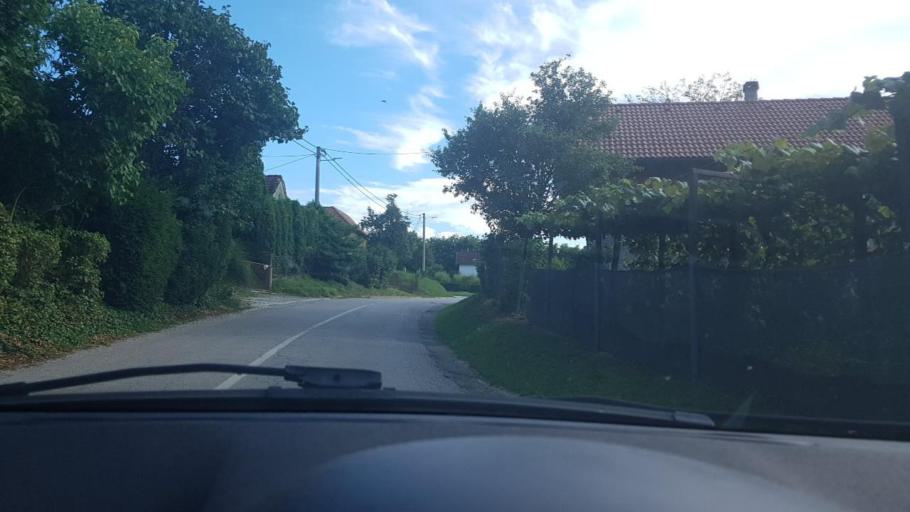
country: HR
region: Varazdinska
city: Tuzno
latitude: 46.2595
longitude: 16.1795
